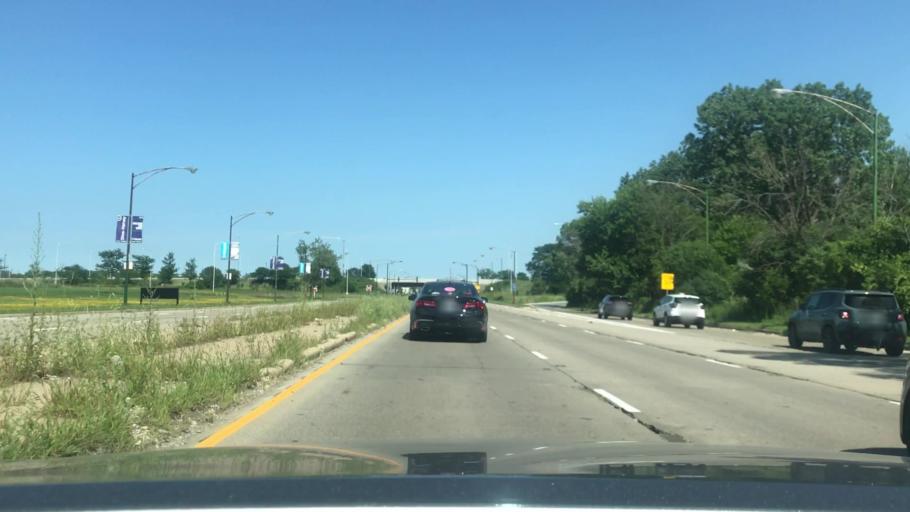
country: US
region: Illinois
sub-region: Cook County
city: Dolton
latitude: 41.7077
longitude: -87.5905
